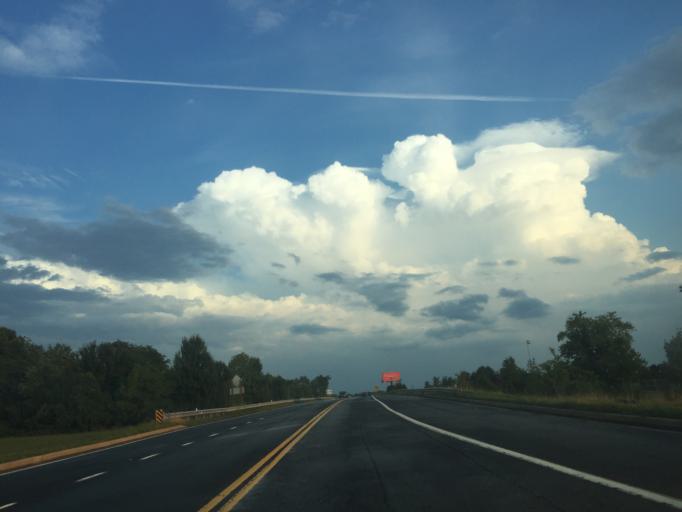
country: US
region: Maryland
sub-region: Harford County
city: Riverside
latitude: 39.4735
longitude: -76.2364
